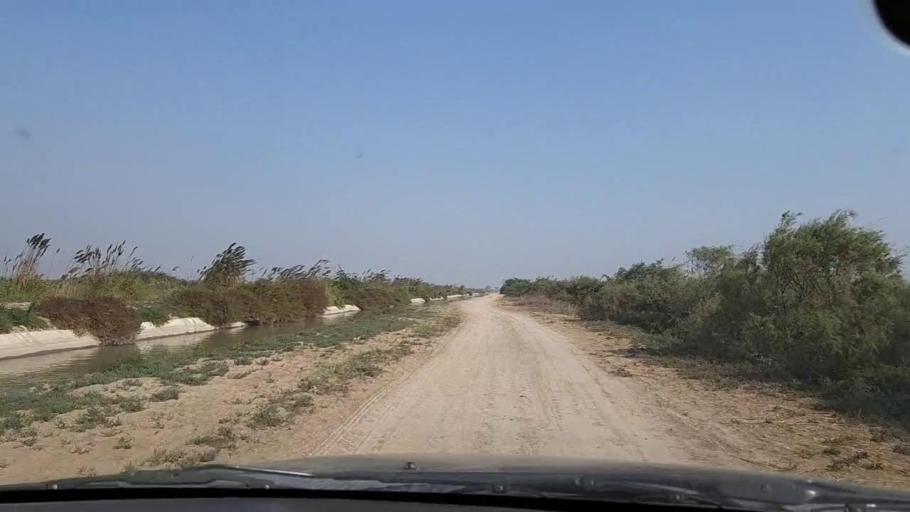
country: PK
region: Sindh
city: Mirpur Sakro
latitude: 24.3419
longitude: 67.7120
